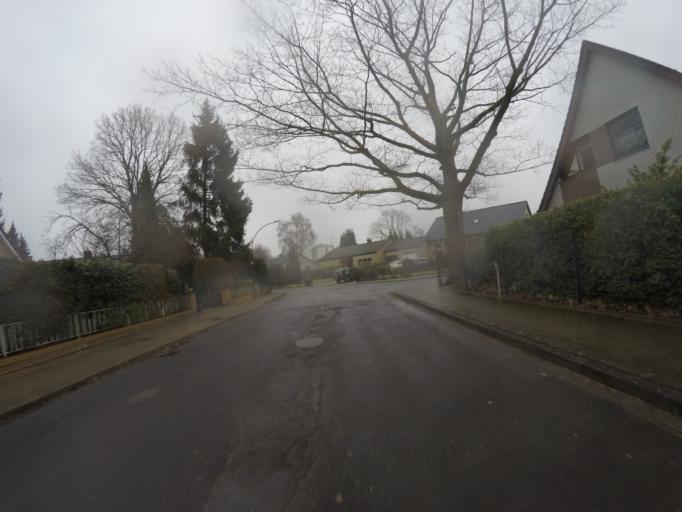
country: DE
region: Schleswig-Holstein
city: Quickborn
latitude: 53.7286
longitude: 9.9226
